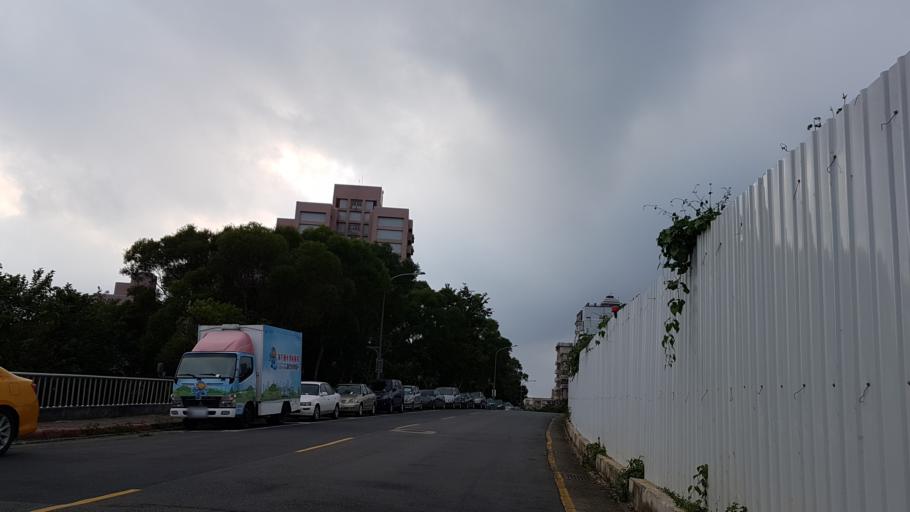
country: TW
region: Taipei
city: Taipei
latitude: 25.0035
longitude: 121.5669
